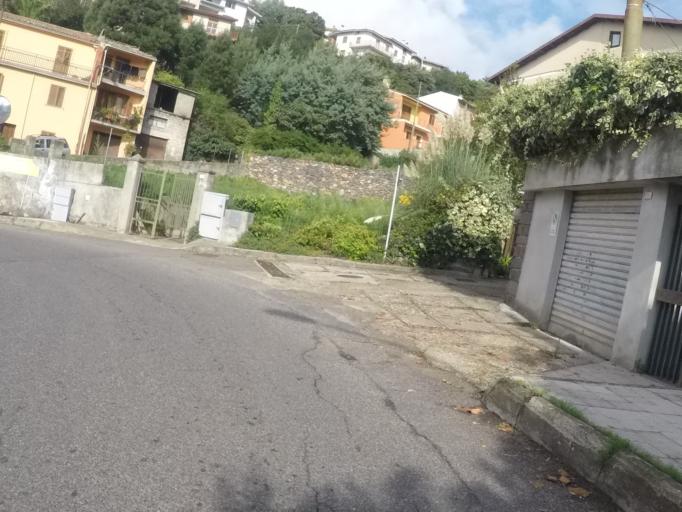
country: IT
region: Sardinia
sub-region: Provincia di Oristano
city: Santu Lussurgiu
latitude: 40.1444
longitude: 8.6510
